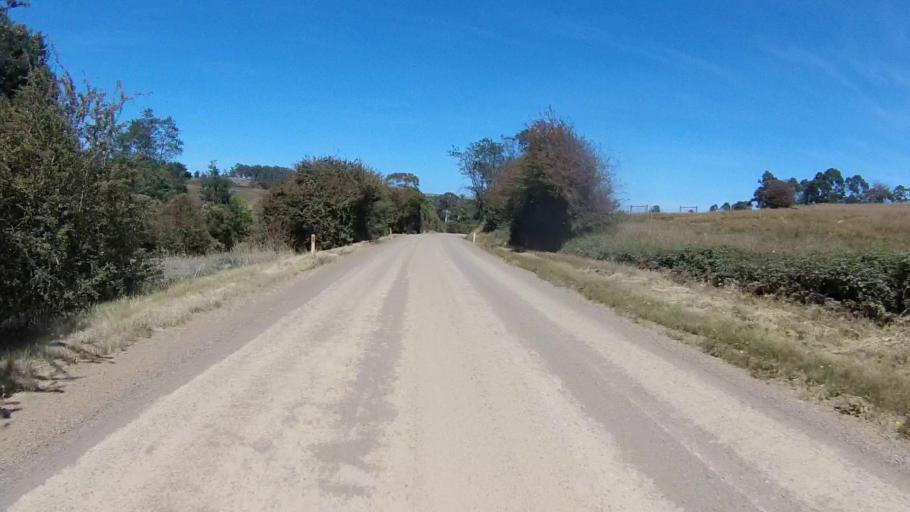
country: AU
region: Tasmania
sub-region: Sorell
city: Sorell
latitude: -42.7562
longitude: 147.6635
